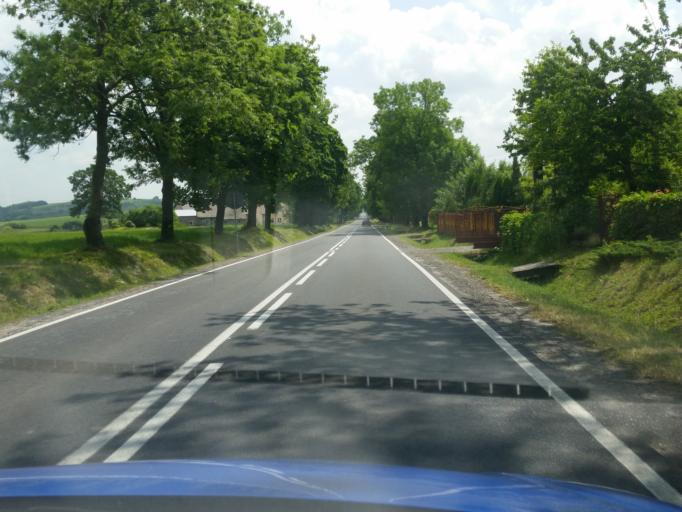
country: PL
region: Lesser Poland Voivodeship
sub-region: Powiat miechowski
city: Miechow
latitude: 50.3580
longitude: 20.0877
